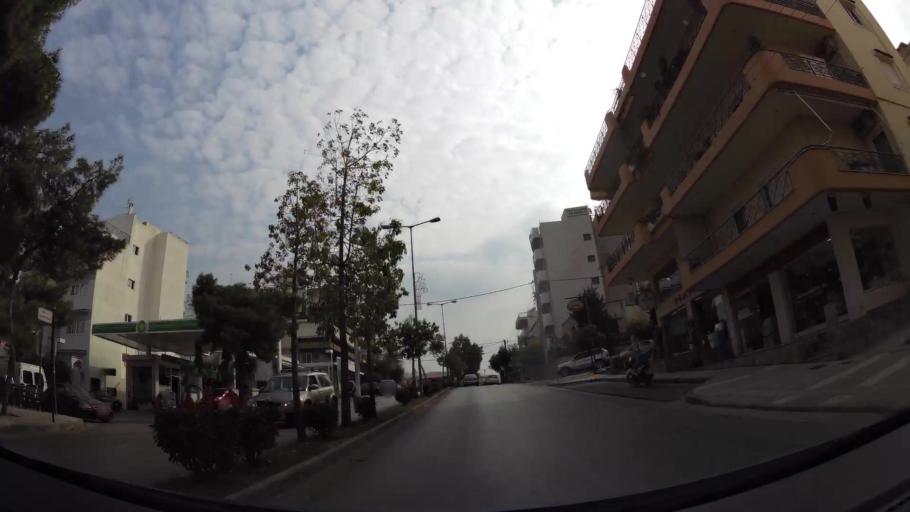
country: GR
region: Attica
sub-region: Nomarchia Athinas
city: Alimos
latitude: 37.9177
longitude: 23.7333
